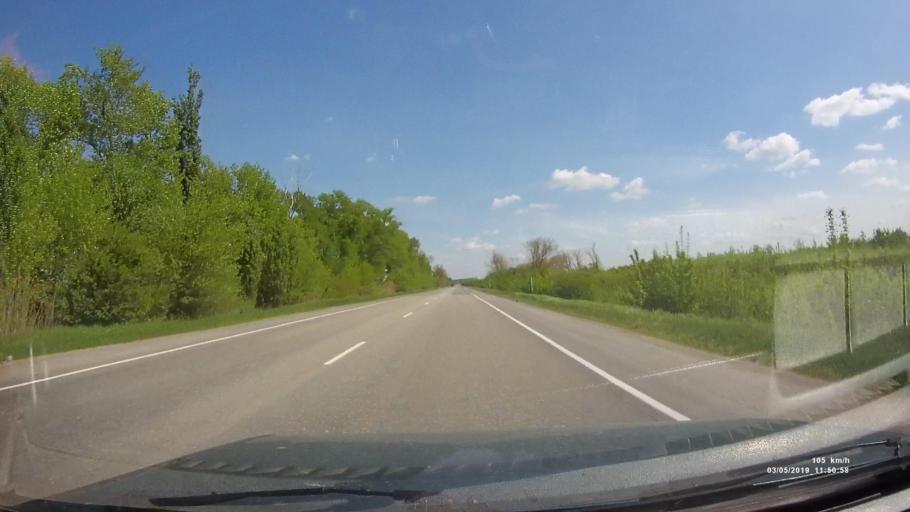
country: RU
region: Rostov
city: Starocherkasskaya
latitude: 47.1561
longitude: 40.2075
